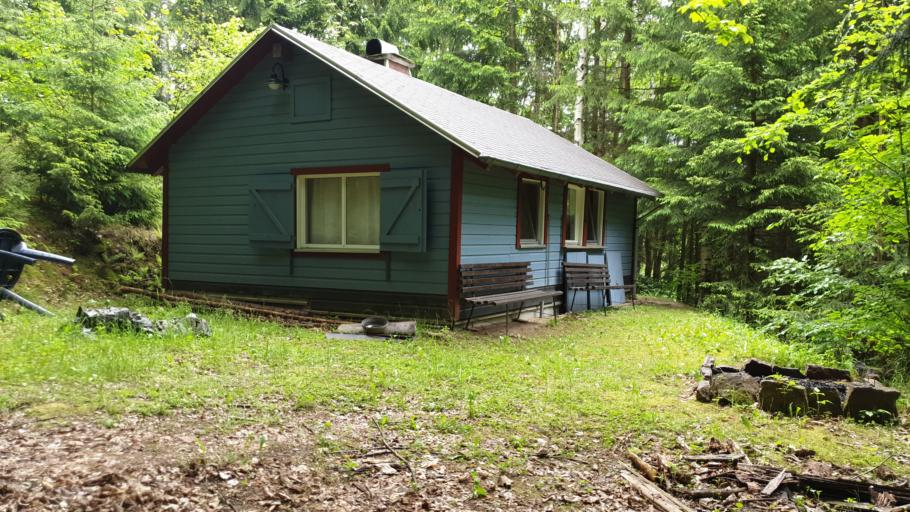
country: DE
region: Saxony
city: Barenstein
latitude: 50.8040
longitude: 13.7732
